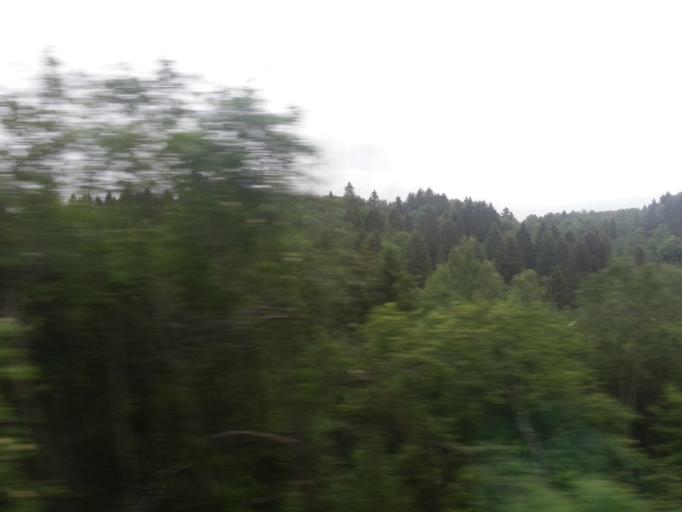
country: NO
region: Sor-Trondelag
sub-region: Trondheim
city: Trondheim
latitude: 63.3690
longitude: 10.3650
